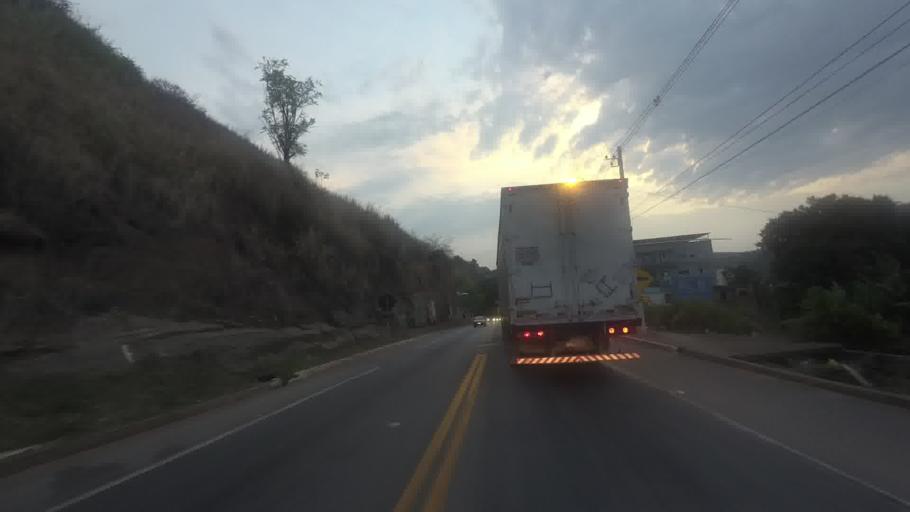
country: BR
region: Minas Gerais
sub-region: Alem Paraiba
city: Alem Paraiba
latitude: -21.8871
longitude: -42.6971
